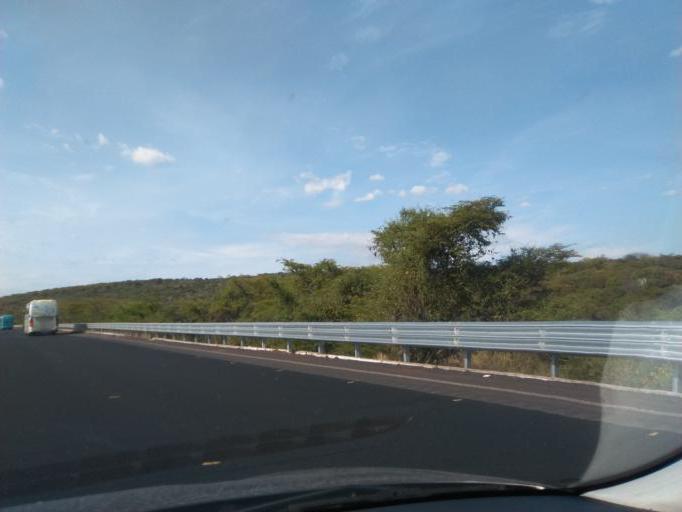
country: MX
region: Morelos
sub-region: Jojutla
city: Higueron
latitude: 18.5489
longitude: -99.2068
